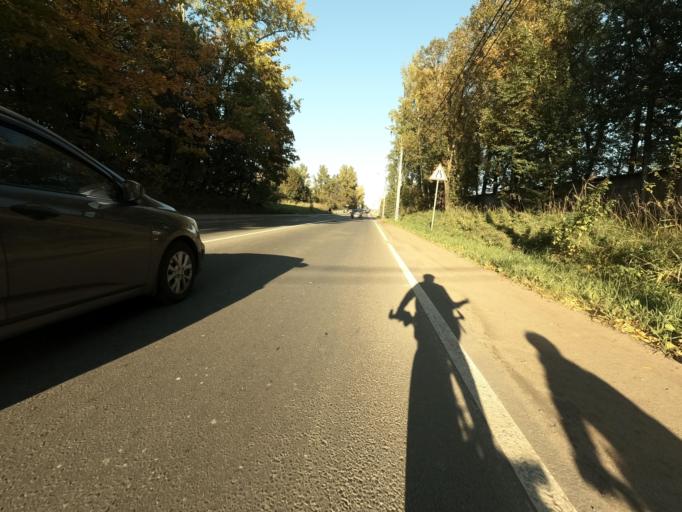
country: RU
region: St.-Petersburg
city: Pontonnyy
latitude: 59.7579
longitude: 30.6198
